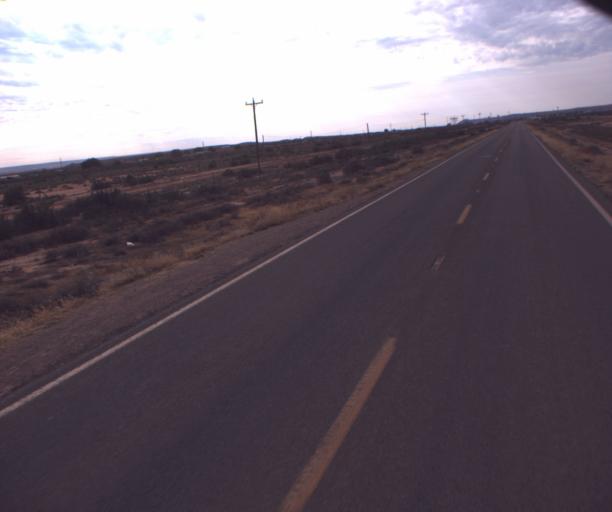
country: US
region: Arizona
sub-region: Apache County
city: Many Farms
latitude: 36.3716
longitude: -109.6130
